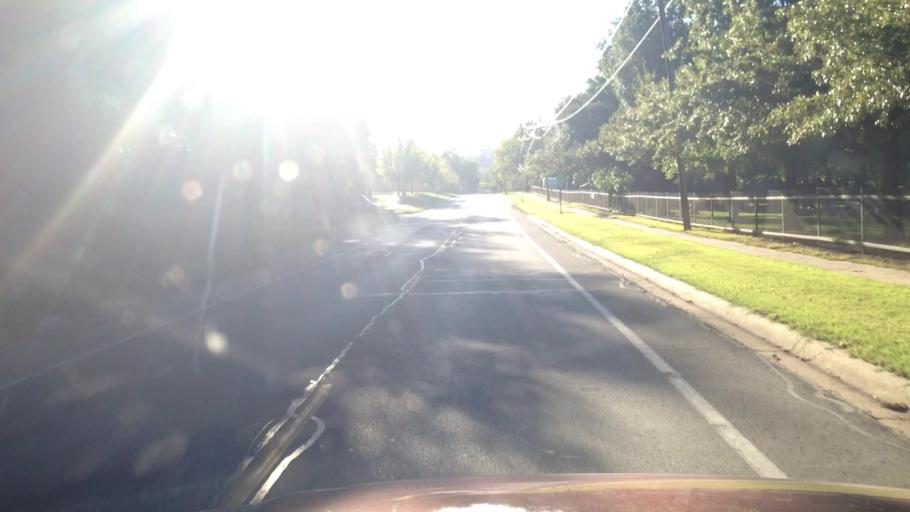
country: US
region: Kansas
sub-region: Douglas County
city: Lawrence
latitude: 38.9570
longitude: -95.2129
